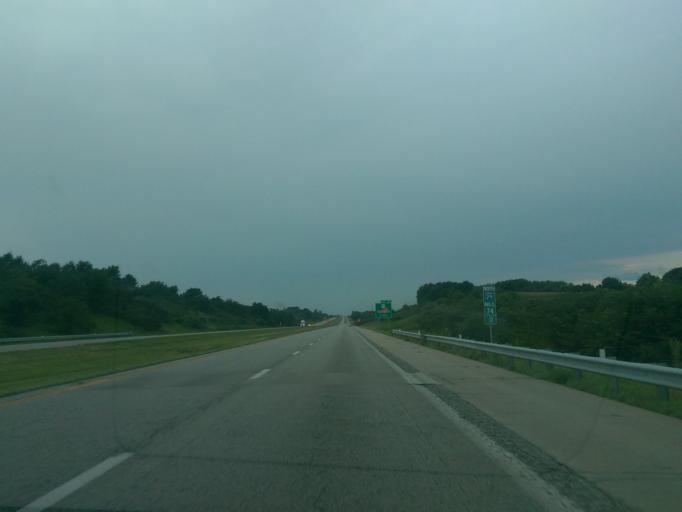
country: US
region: Missouri
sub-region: Holt County
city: Oregon
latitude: 40.0315
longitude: -95.1134
